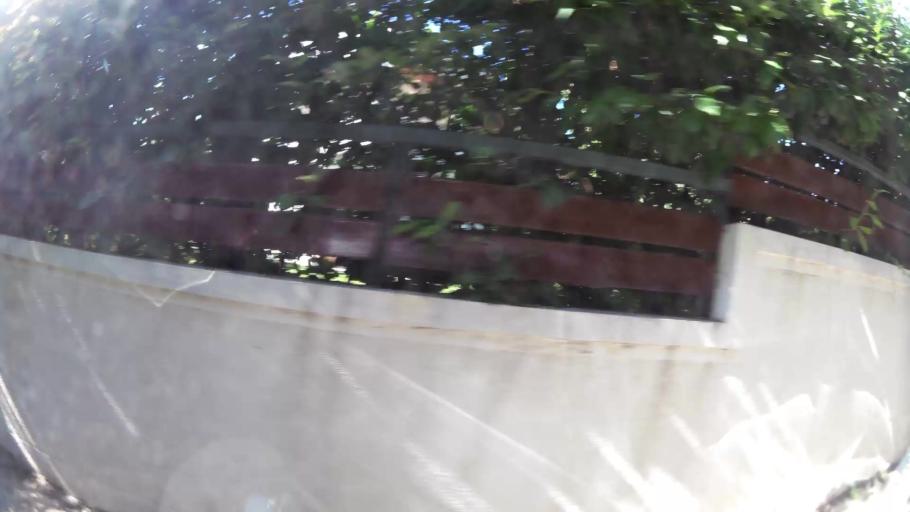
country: GR
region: Attica
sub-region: Nomarchia Athinas
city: Ekali
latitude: 38.1175
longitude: 23.8368
